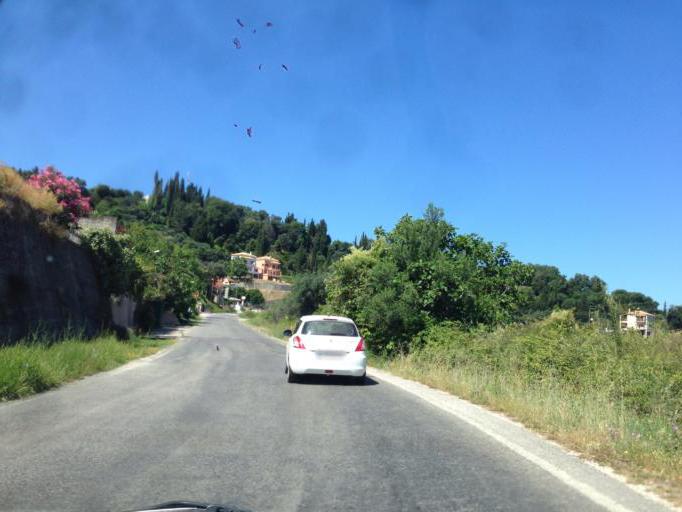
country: GR
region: Ionian Islands
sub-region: Nomos Kerkyras
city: Acharavi
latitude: 39.7854
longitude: 19.7466
